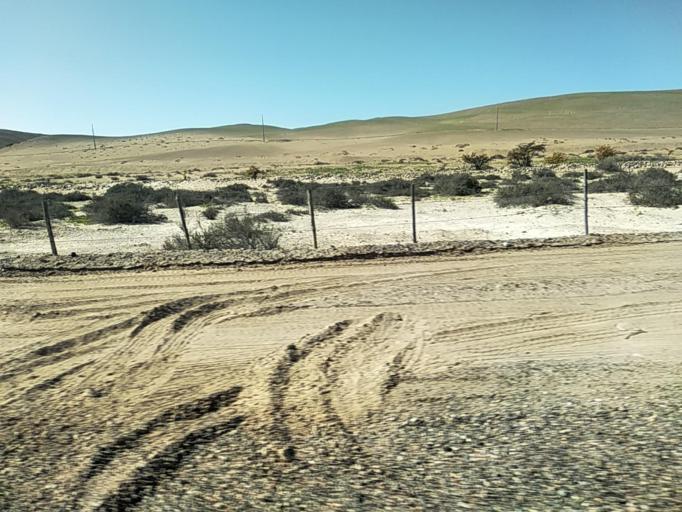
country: CL
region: Atacama
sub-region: Provincia de Copiapo
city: Copiapo
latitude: -27.3454
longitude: -70.7449
